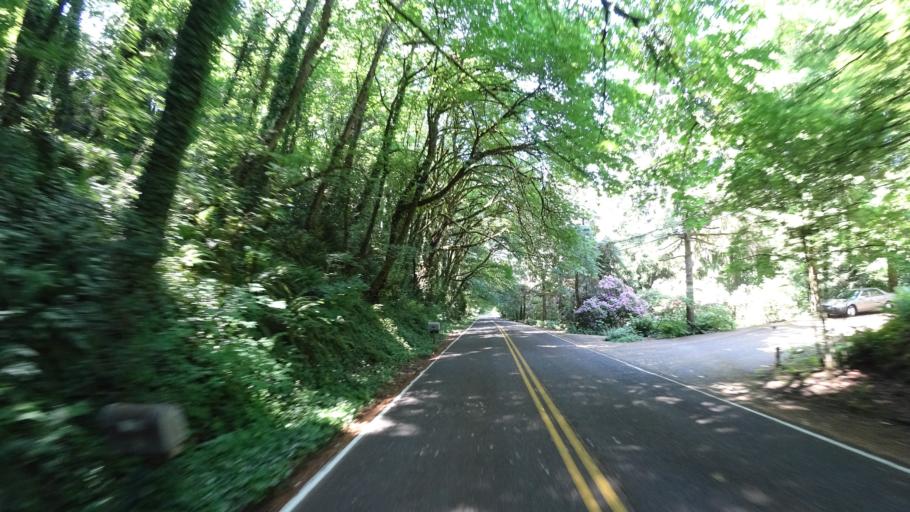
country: US
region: Oregon
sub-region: Clackamas County
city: Lake Oswego
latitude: 45.4418
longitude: -122.6957
